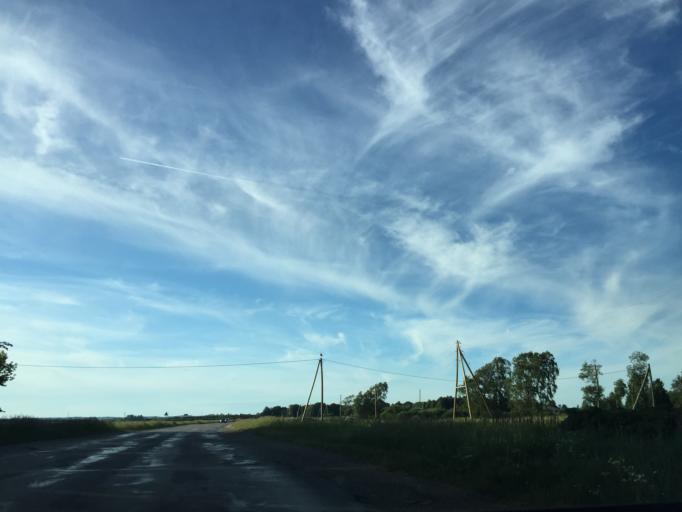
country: LV
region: Ventspils
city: Ventspils
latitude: 57.3082
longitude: 21.5568
